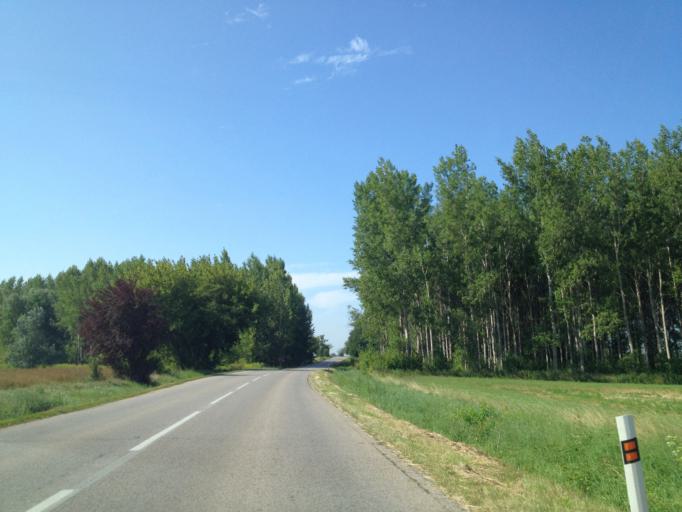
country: SK
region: Nitriansky
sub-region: Okres Komarno
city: Hurbanovo
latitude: 47.8277
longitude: 18.2350
